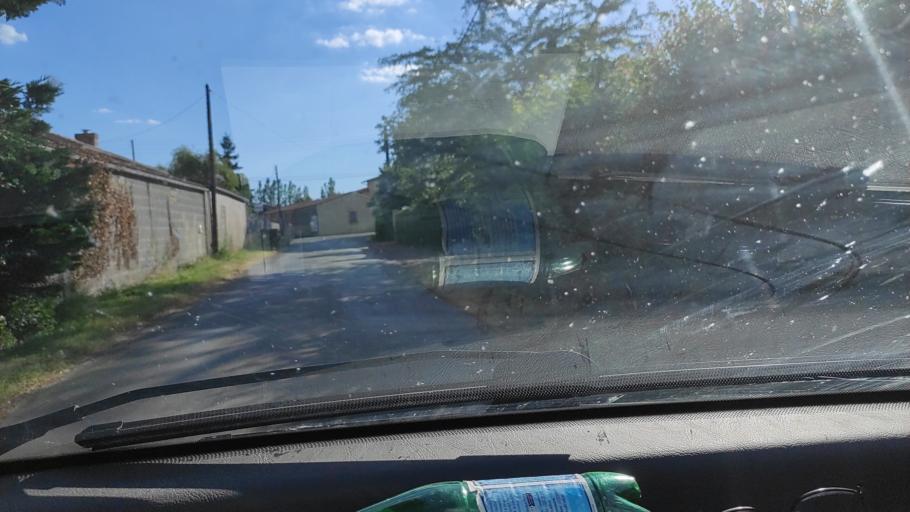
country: FR
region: Poitou-Charentes
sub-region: Departement des Deux-Sevres
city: Saint-Varent
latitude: 46.8576
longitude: -0.1995
